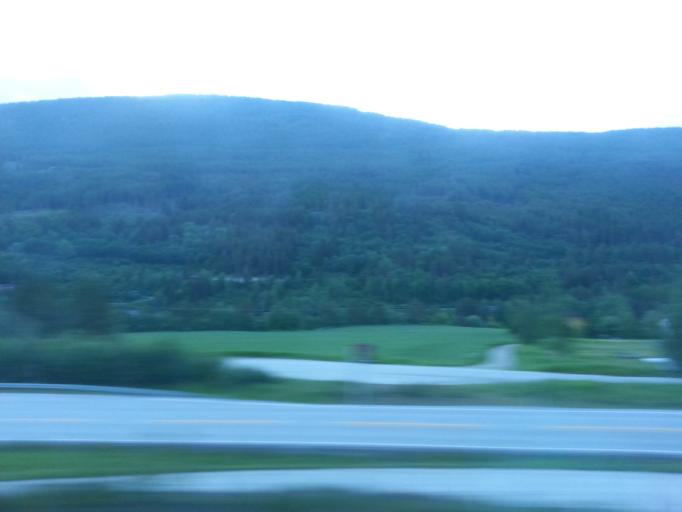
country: NO
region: Oppland
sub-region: Dovre
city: Dovre
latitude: 61.9157
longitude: 9.3559
